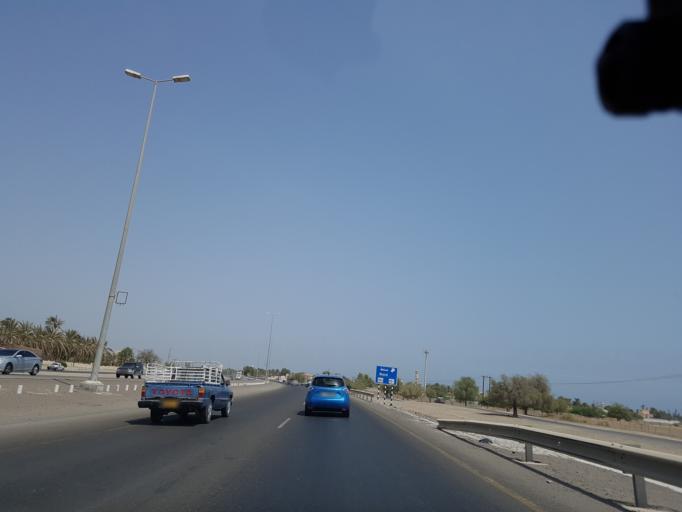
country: OM
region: Al Batinah
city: Saham
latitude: 24.1962
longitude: 56.8588
